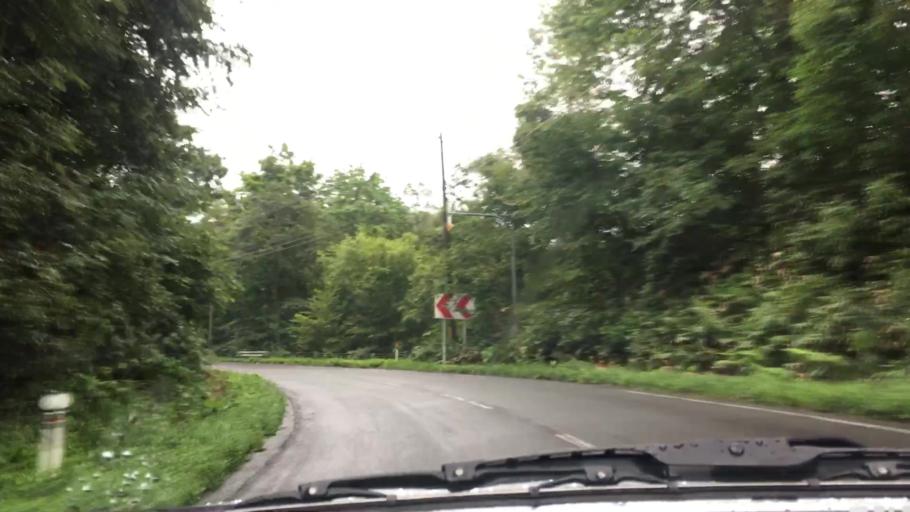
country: JP
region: Hokkaido
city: Niseko Town
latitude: 42.6294
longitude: 140.7199
